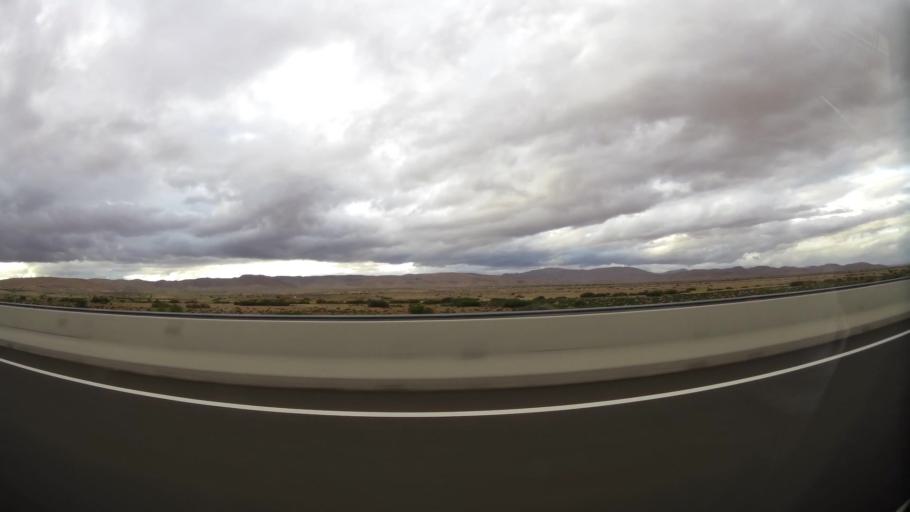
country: MA
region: Taza-Al Hoceima-Taounate
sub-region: Taza
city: Guercif
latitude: 34.3053
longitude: -3.6404
